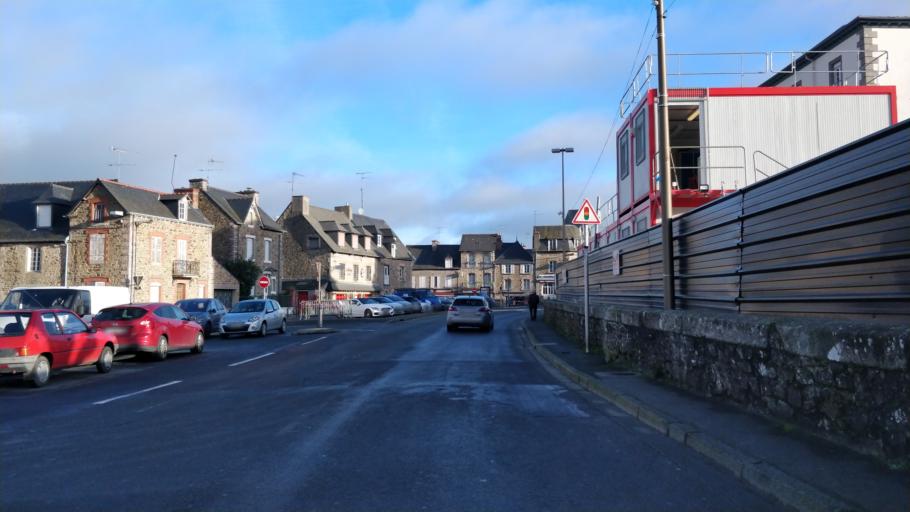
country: FR
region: Brittany
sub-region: Departement des Cotes-d'Armor
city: Lamballe
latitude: 48.4706
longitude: -2.5166
